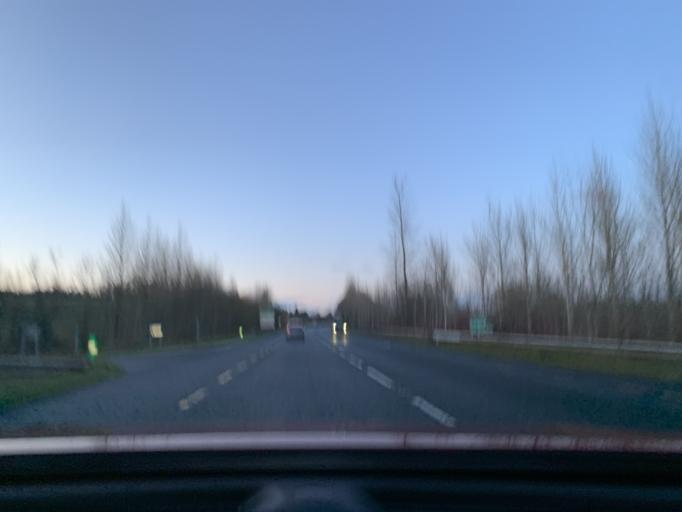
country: IE
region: Connaught
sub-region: County Leitrim
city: Carrick-on-Shannon
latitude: 53.9252
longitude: -7.9960
